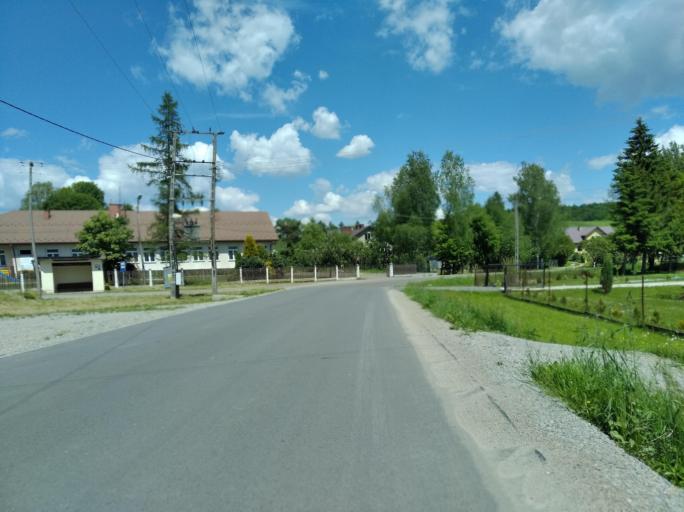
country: PL
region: Subcarpathian Voivodeship
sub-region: Powiat krosnienski
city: Leki
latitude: 49.7826
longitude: 21.6111
